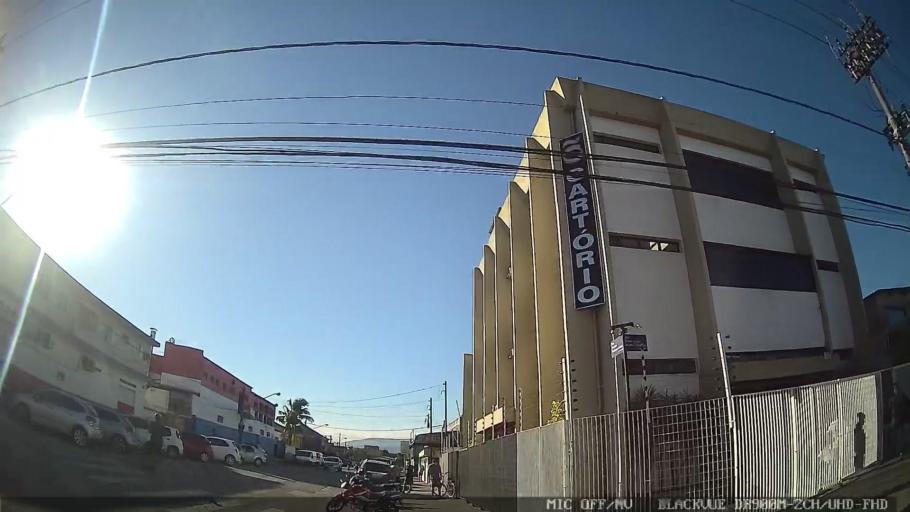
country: BR
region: Sao Paulo
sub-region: Santos
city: Santos
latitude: -23.9565
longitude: -46.2920
